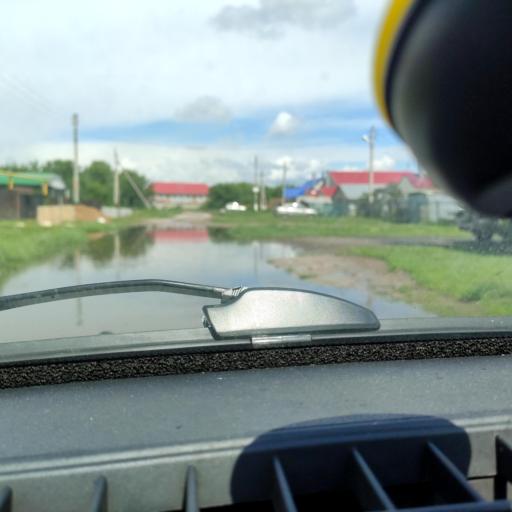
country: RU
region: Samara
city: Zhigulevsk
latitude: 53.5542
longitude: 49.5236
